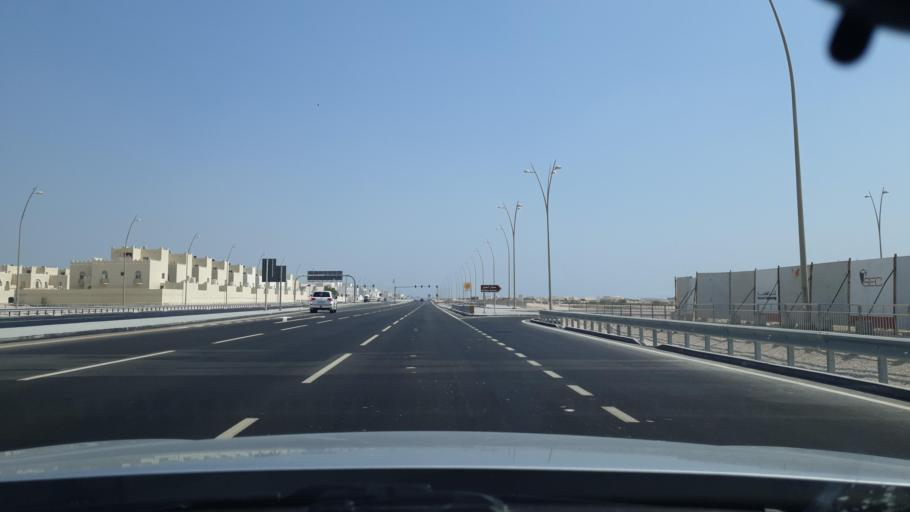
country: QA
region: Al Khawr
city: Al Khawr
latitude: 25.6639
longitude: 51.5039
